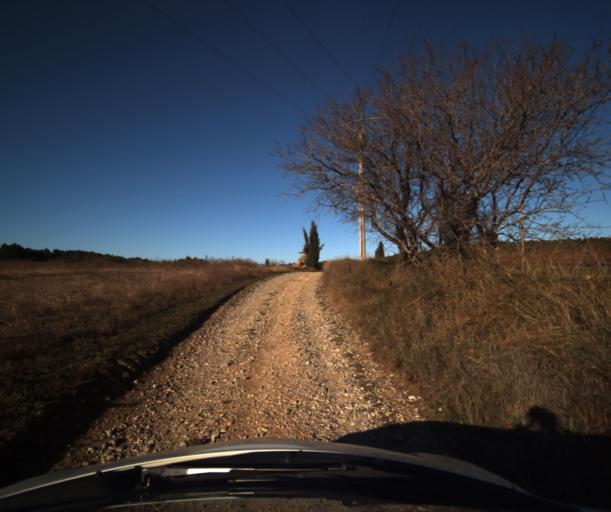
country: FR
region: Provence-Alpes-Cote d'Azur
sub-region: Departement du Vaucluse
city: Ansouis
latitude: 43.7204
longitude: 5.4873
